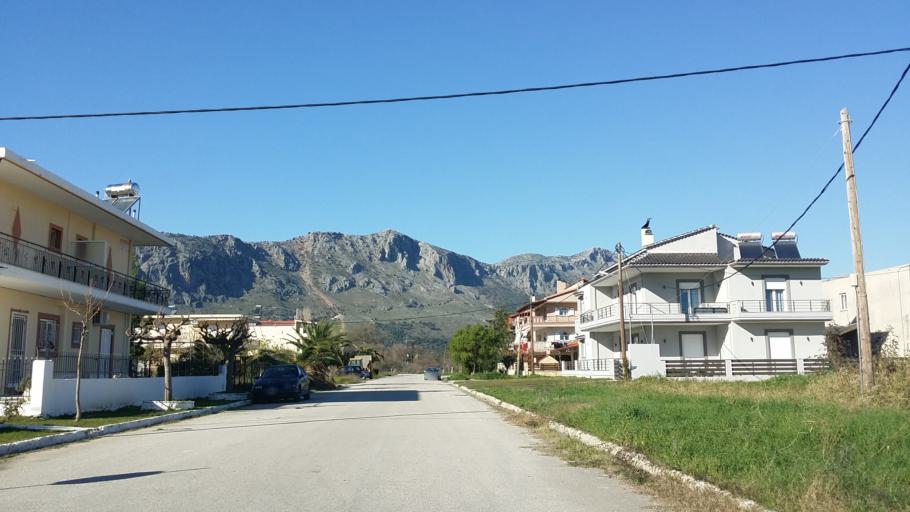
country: GR
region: West Greece
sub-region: Nomos Aitolias kai Akarnanias
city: Kandila
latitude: 38.6710
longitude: 20.9493
